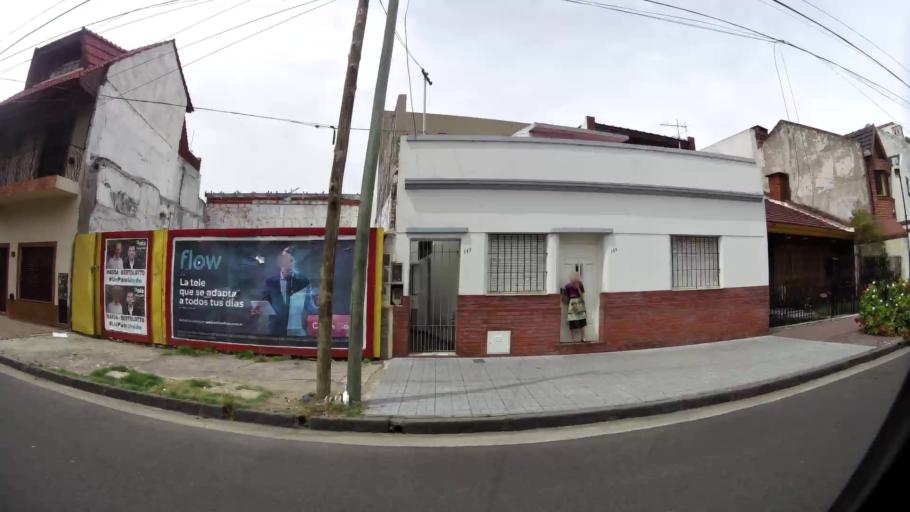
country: AR
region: Buenos Aires
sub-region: Partido de Avellaneda
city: Avellaneda
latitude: -34.6668
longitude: -58.3547
